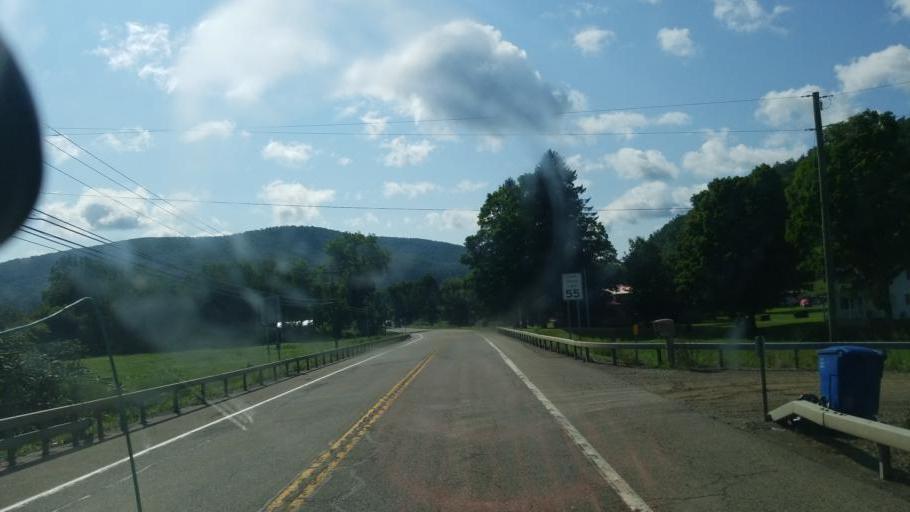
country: US
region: New York
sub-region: Steuben County
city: Canisteo
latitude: 42.2652
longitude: -77.5938
